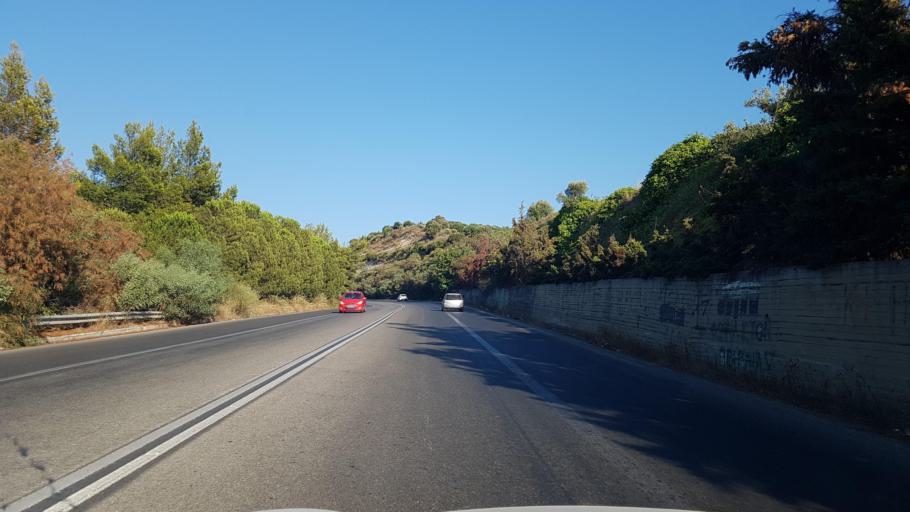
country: GR
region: Crete
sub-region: Nomos Chanias
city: Gerani
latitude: 35.5147
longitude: 23.8296
